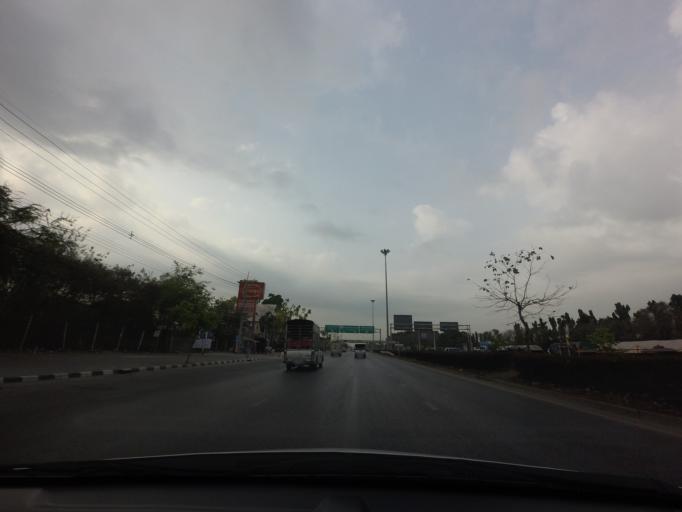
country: TH
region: Bangkok
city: Thawi Watthana
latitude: 13.7823
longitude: 100.3280
